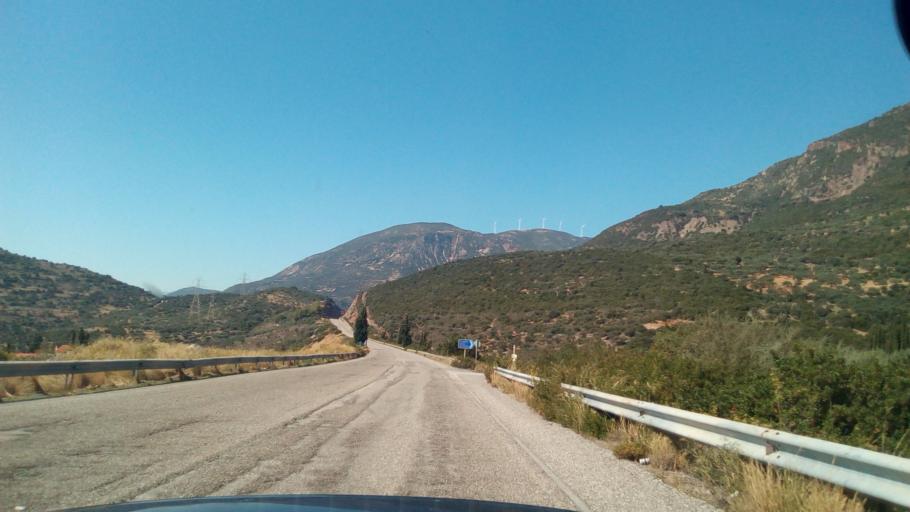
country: GR
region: West Greece
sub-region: Nomos Achaias
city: Selianitika
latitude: 38.3844
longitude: 22.0878
